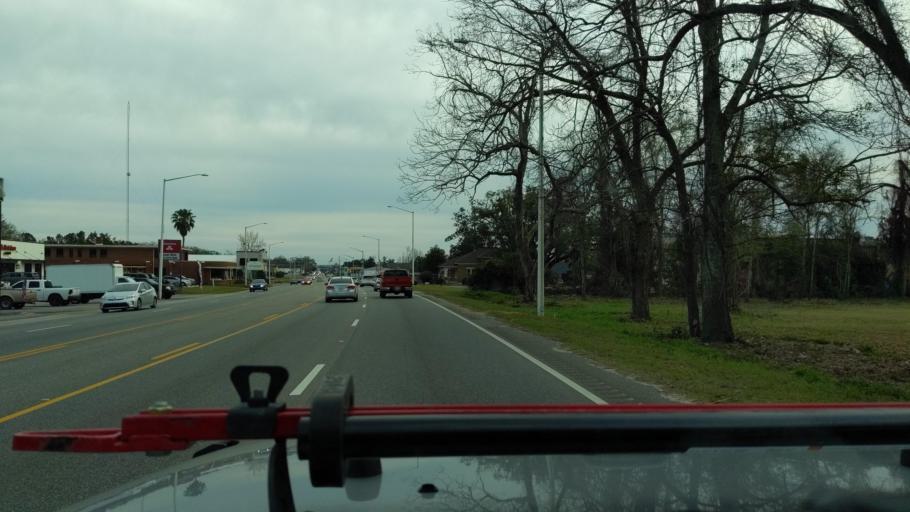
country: US
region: Alabama
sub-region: Baldwin County
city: Foley
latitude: 30.4162
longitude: -87.6838
